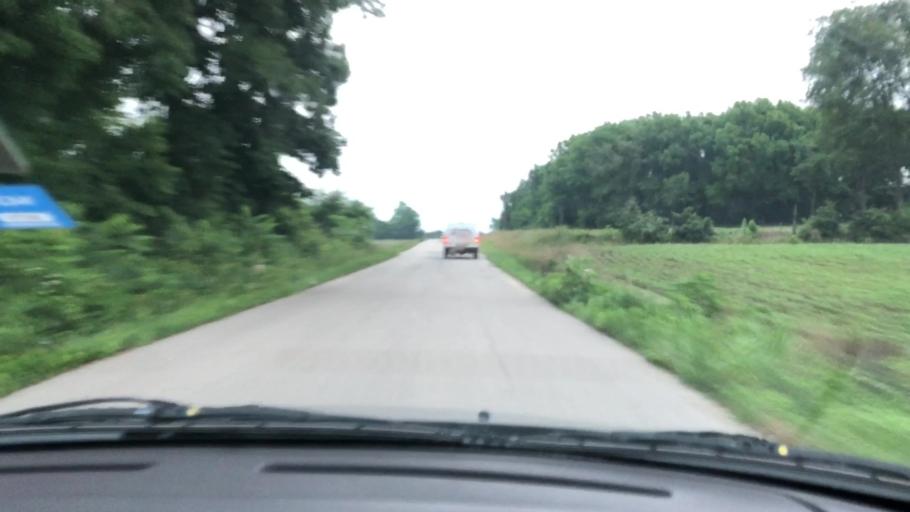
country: US
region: Indiana
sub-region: Greene County
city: Linton
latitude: 38.9800
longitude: -87.2981
